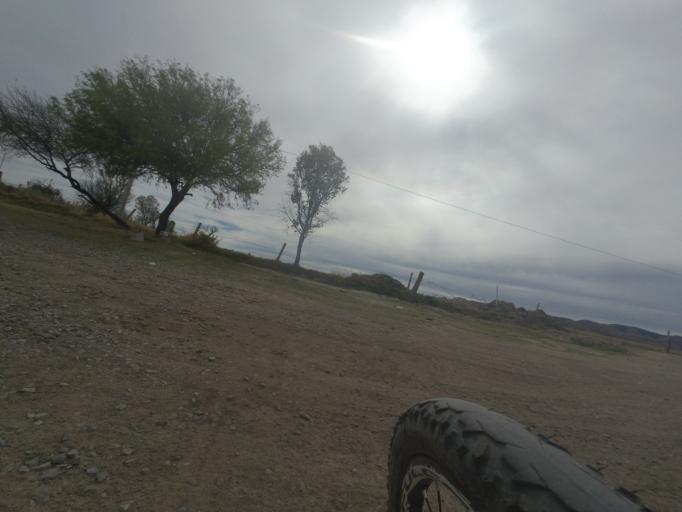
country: MX
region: Aguascalientes
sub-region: Aguascalientes
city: La Loma de los Negritos
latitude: 21.8444
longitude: -102.3569
